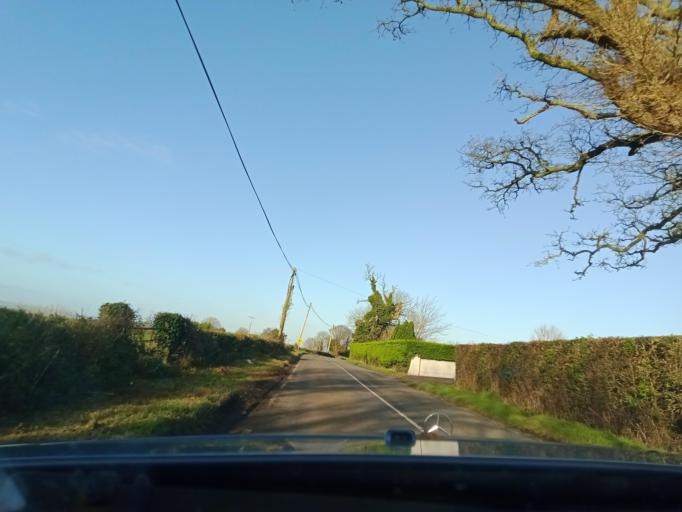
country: IE
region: Leinster
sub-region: Kilkenny
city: Callan
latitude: 52.5099
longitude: -7.3845
